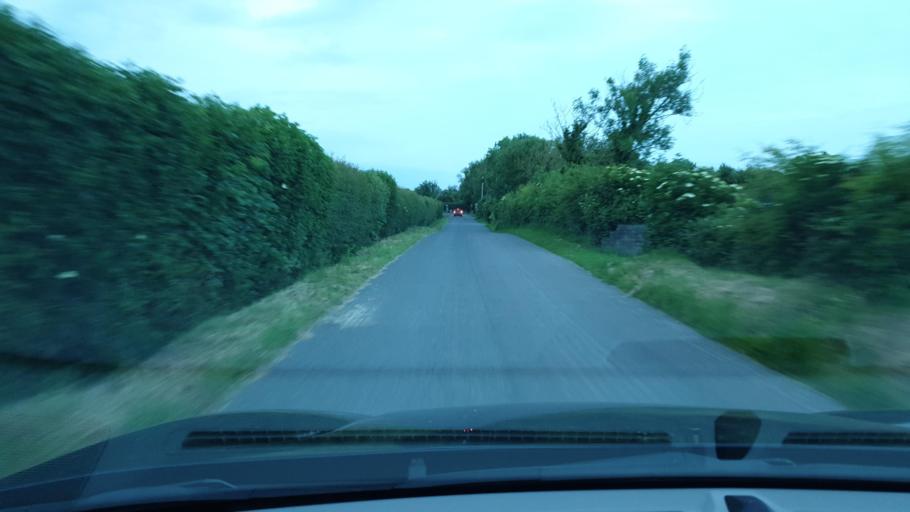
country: IE
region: Leinster
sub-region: An Mhi
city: Ashbourne
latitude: 53.5791
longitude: -6.3496
